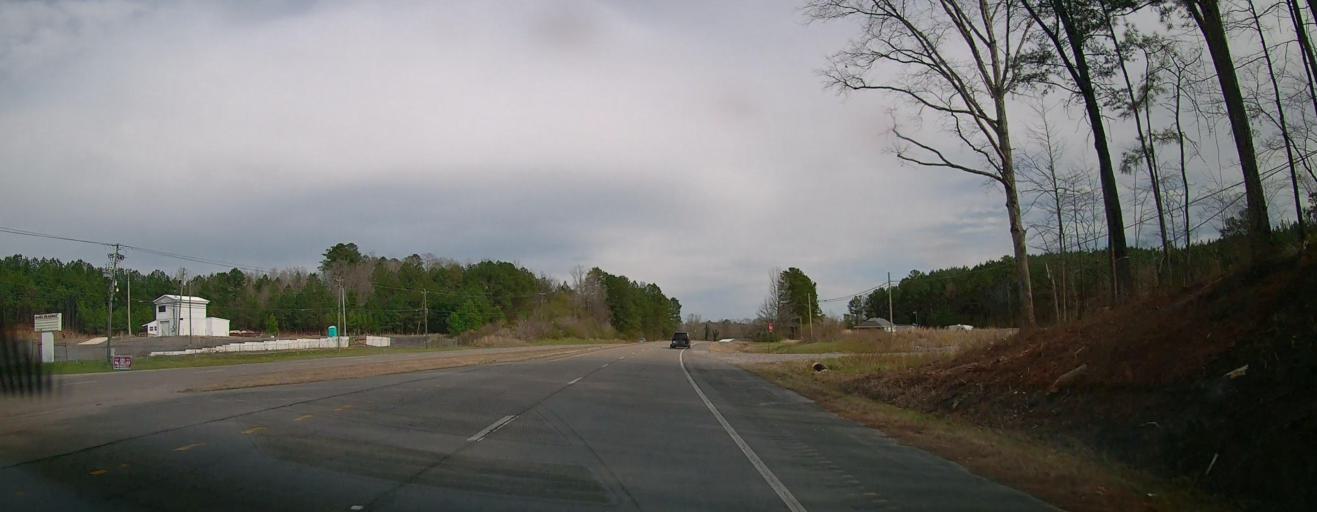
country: US
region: Alabama
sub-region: Walker County
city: Sumiton
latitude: 33.7937
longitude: -87.0967
